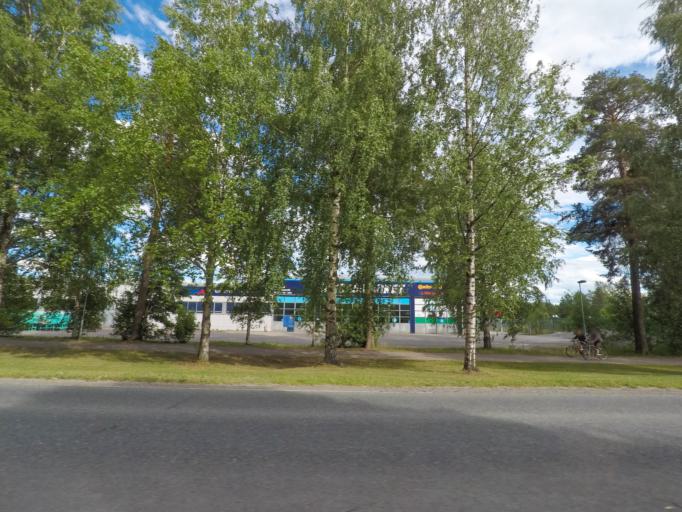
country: FI
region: Paijanne Tavastia
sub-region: Lahti
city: Lahti
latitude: 60.9679
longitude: 25.6272
